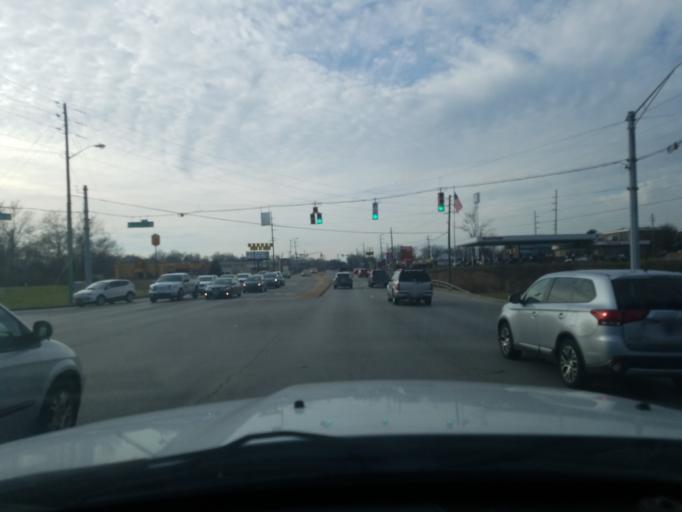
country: US
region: Indiana
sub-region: Marion County
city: Southport
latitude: 39.6656
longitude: -86.0948
